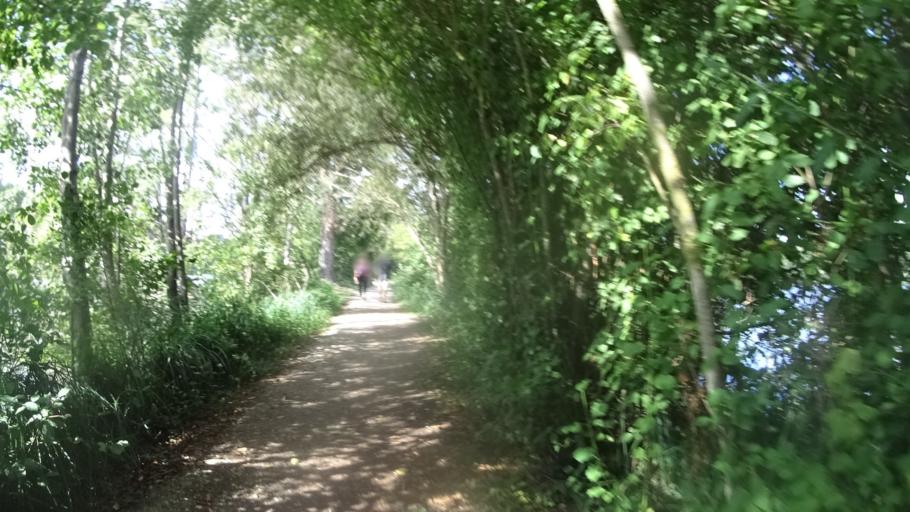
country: FR
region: Ile-de-France
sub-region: Departement de l'Essonne
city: Vert-le-Petit
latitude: 48.5400
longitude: 2.3706
